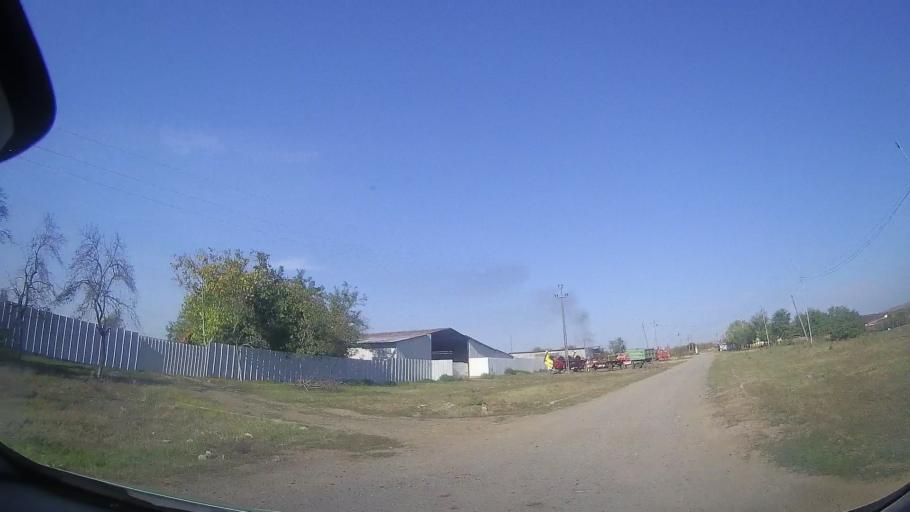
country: RO
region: Timis
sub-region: Comuna Topolovatu Mare
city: Topolovatu Mare
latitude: 45.8190
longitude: 21.5782
